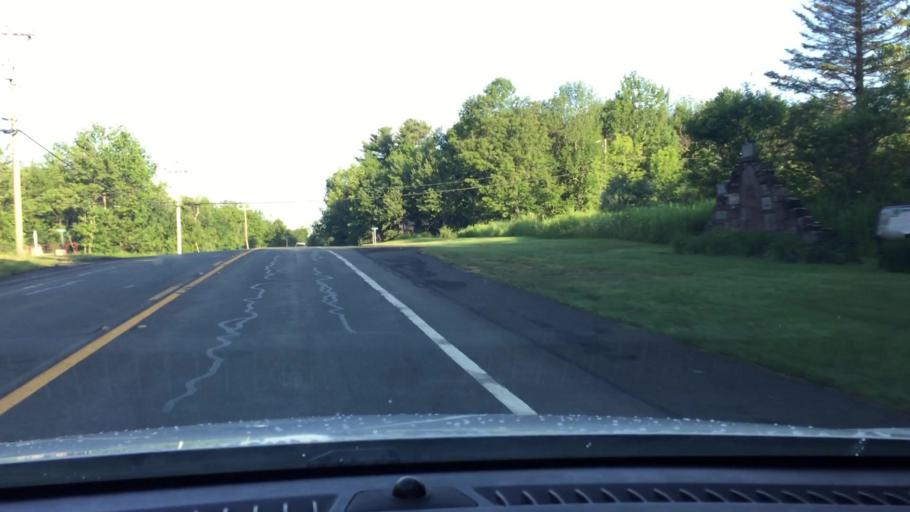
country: US
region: Massachusetts
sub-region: Berkshire County
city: Otis
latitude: 42.2586
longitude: -73.0858
